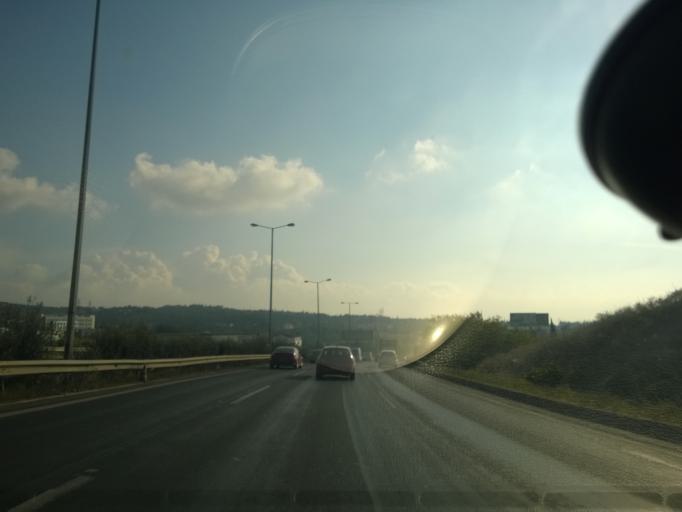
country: GR
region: Central Macedonia
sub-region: Nomos Thessalonikis
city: Pylaia
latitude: 40.6100
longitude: 22.9999
